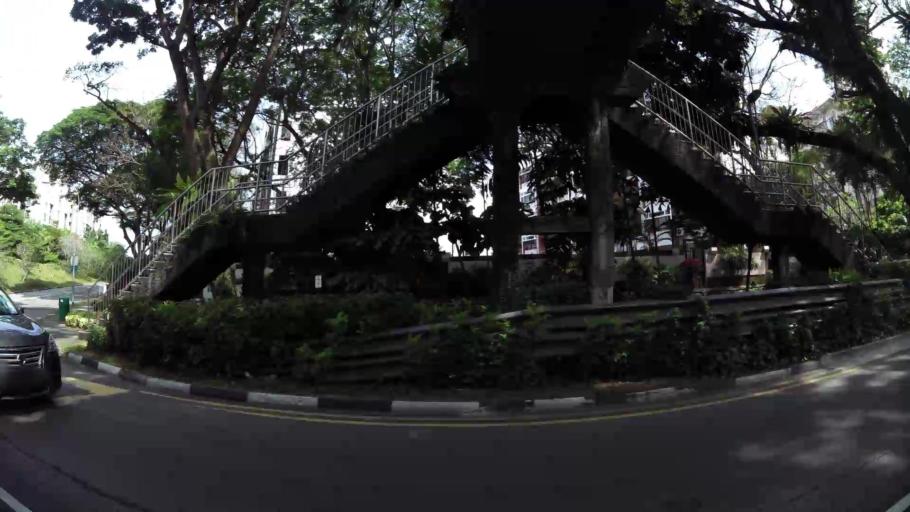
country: SG
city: Singapore
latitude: 1.3368
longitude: 103.7816
